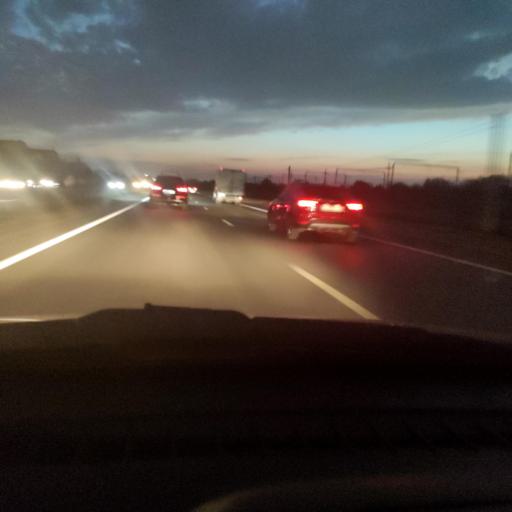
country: RU
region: Samara
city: Tol'yatti
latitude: 53.5741
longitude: 49.3916
